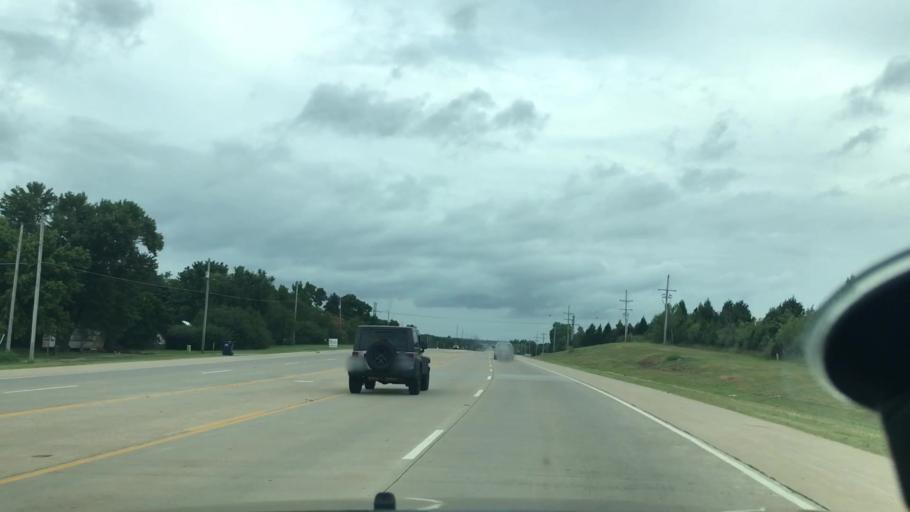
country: US
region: Oklahoma
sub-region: Seminole County
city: Seminole
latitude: 35.2681
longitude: -96.6709
